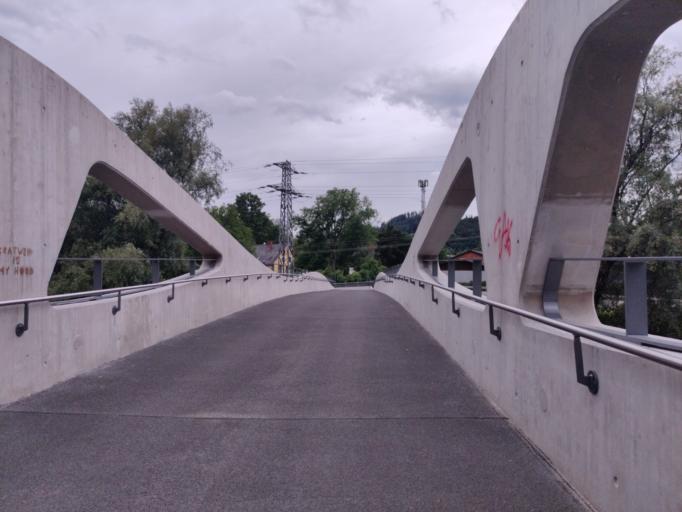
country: AT
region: Styria
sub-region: Politischer Bezirk Graz-Umgebung
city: Gratwein
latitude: 47.1321
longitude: 15.3250
